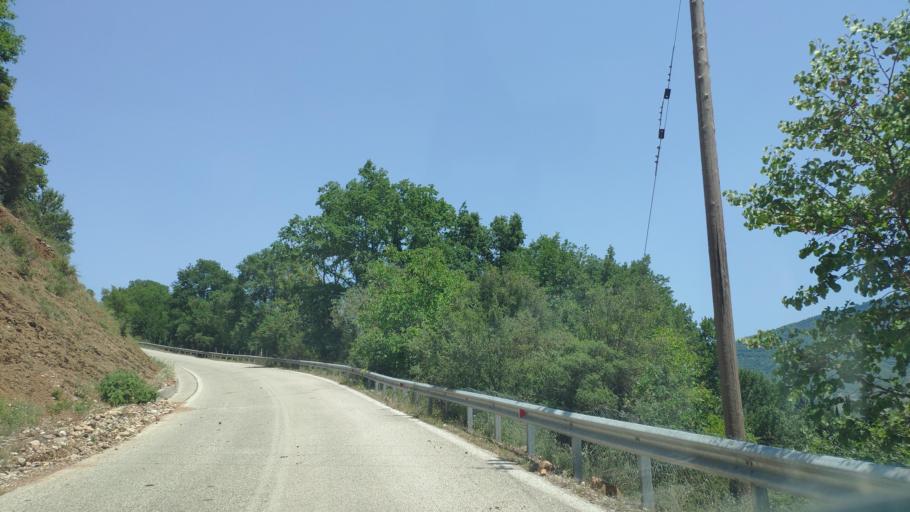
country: GR
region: Epirus
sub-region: Nomos Artas
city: Ano Kalentini
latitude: 39.2173
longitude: 21.3491
